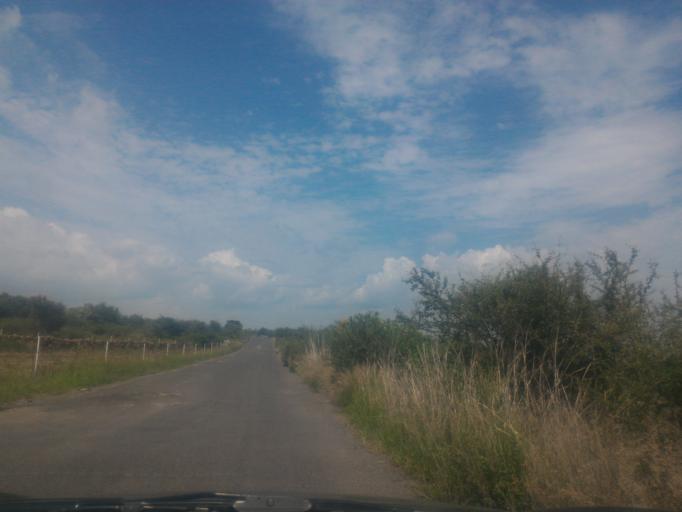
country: MX
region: Guanajuato
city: Ciudad Manuel Doblado
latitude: 20.8341
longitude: -102.0139
